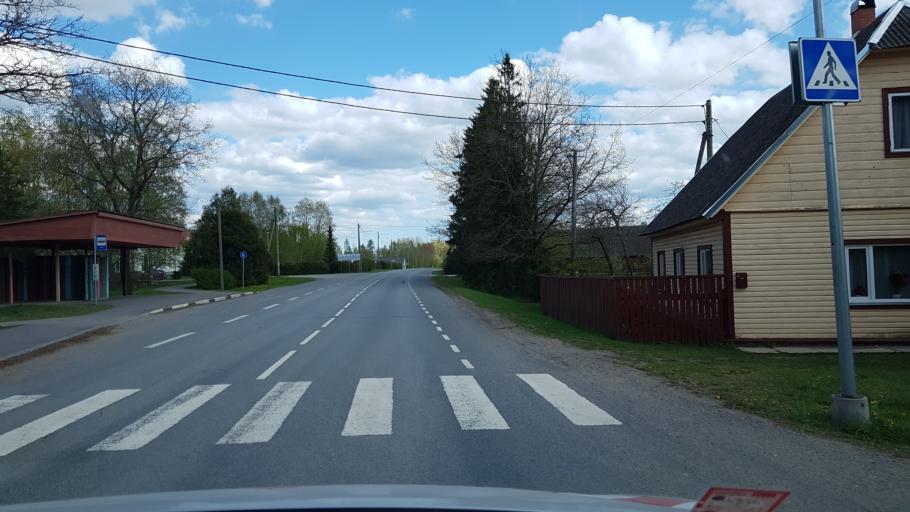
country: EE
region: Polvamaa
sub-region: Polva linn
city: Polva
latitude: 58.2830
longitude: 27.0485
